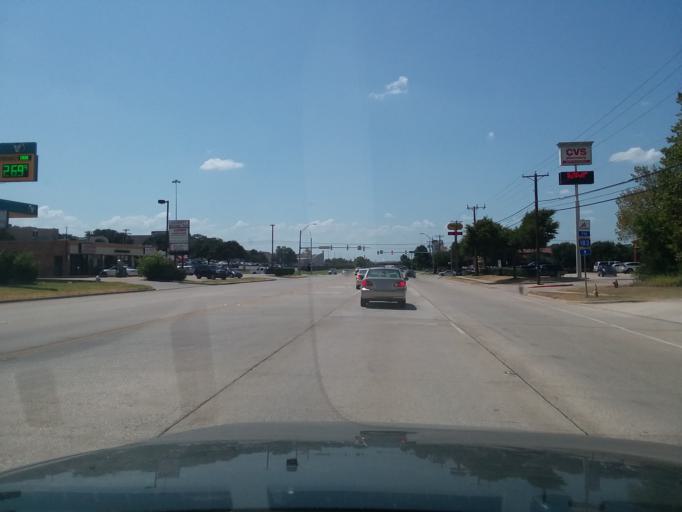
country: US
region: Texas
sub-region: Tarrant County
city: Euless
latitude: 32.8454
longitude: -97.0999
